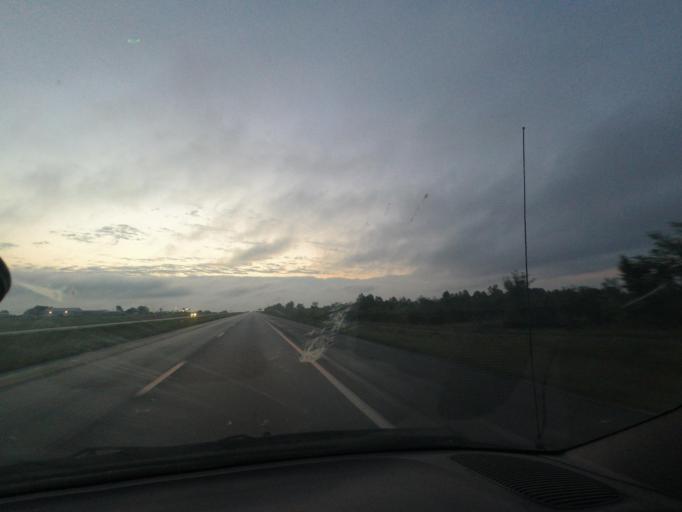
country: US
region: Missouri
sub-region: Linn County
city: Brookfield
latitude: 39.7626
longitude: -93.0155
